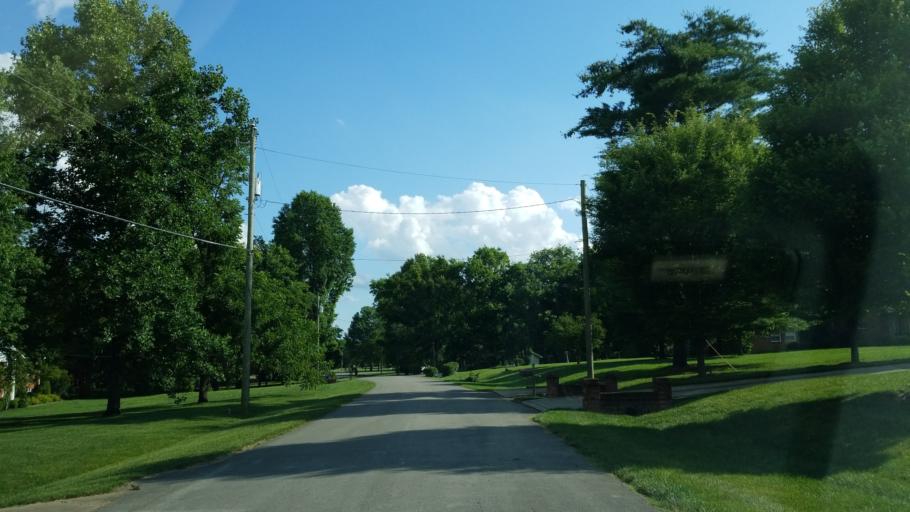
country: US
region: Tennessee
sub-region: Williamson County
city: Brentwood
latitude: 36.0270
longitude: -86.7978
